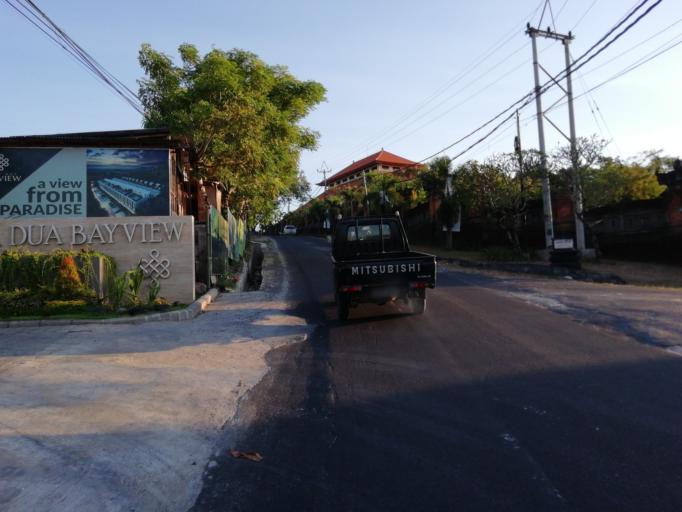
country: ID
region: Bali
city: Bualu
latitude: -8.8098
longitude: 115.1937
